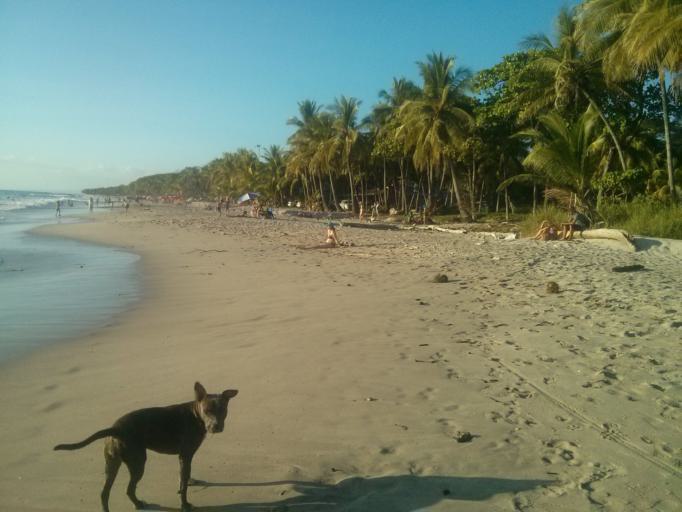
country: CR
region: Guanacaste
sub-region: Canton de Nandayure
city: Bejuco
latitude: 9.6255
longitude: -85.1512
